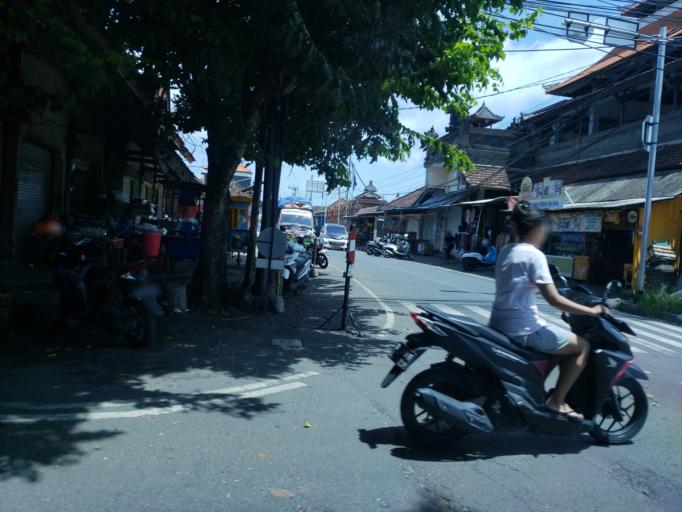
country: ID
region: Bali
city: Kelanabian
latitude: -8.7707
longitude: 115.1732
